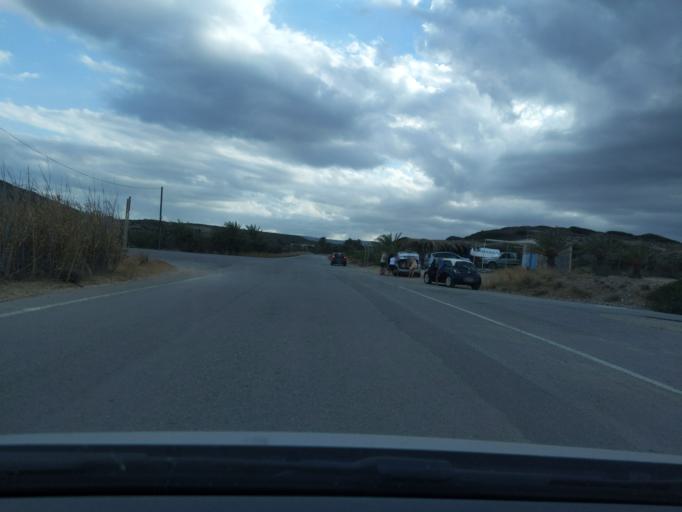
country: GR
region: Crete
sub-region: Nomos Lasithiou
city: Palekastro
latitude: 35.2544
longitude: 26.2533
